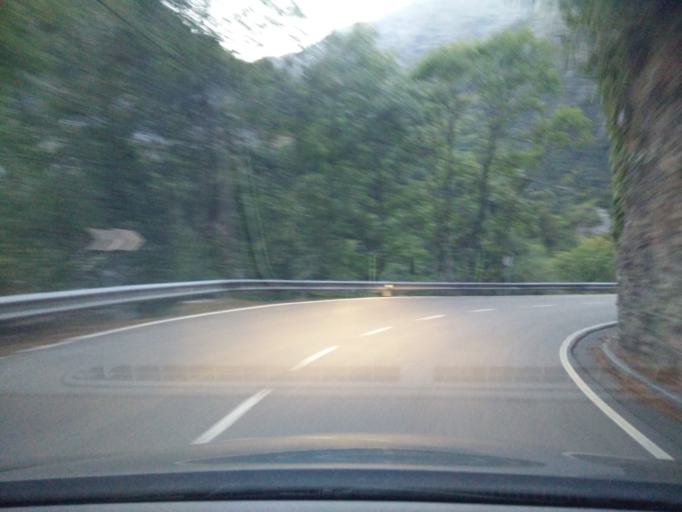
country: ES
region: Asturias
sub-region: Province of Asturias
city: Amieva
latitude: 43.2110
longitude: -5.0917
